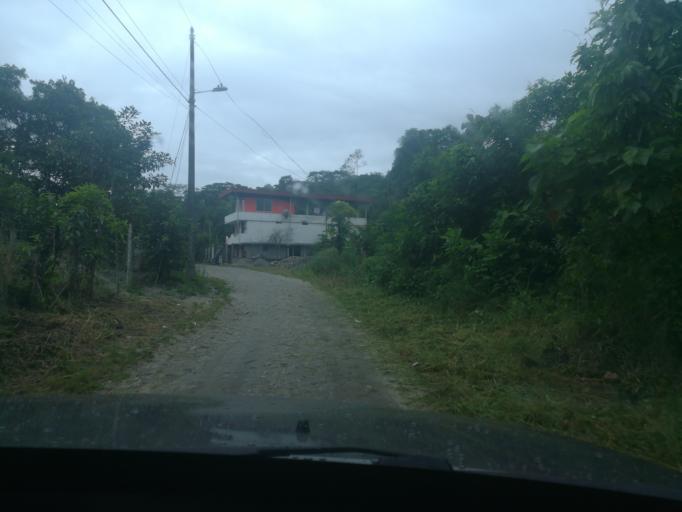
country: EC
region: Napo
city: Tena
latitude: -1.0488
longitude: -77.7979
